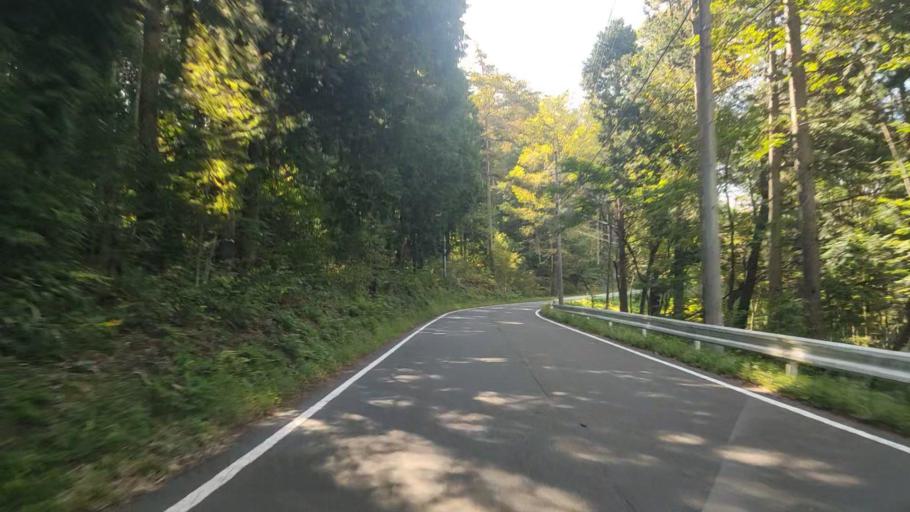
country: JP
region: Gunma
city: Nakanojomachi
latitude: 36.6043
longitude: 138.6843
